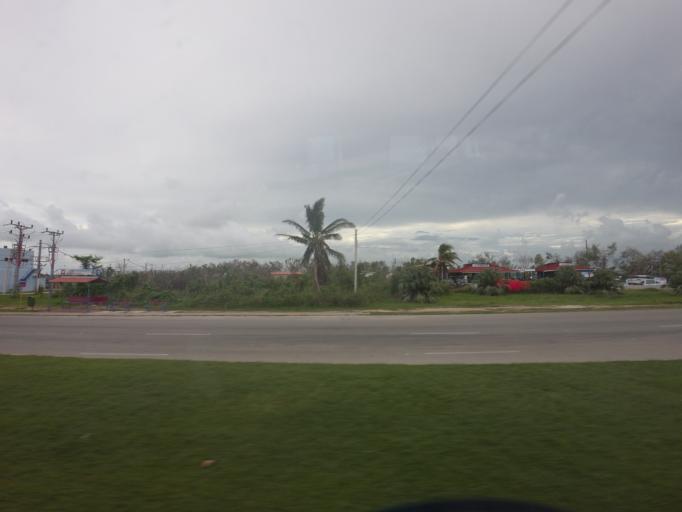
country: CU
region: Matanzas
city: Varadero
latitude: 23.1755
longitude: -81.2015
